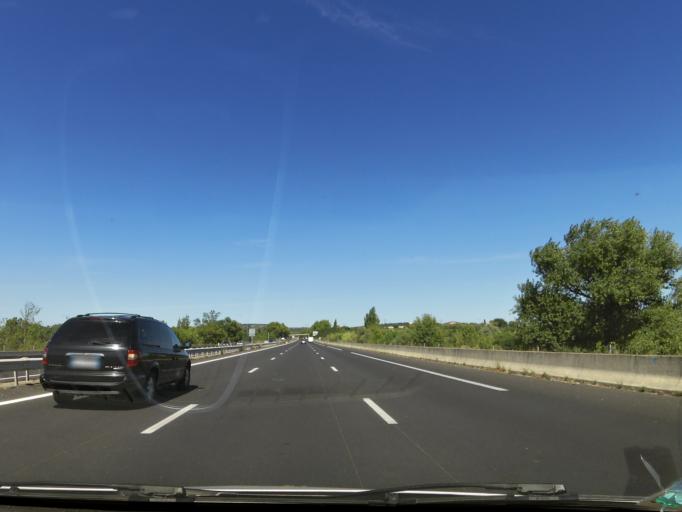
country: FR
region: Languedoc-Roussillon
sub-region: Departement du Gard
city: Remoulins
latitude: 43.9221
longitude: 4.5835
